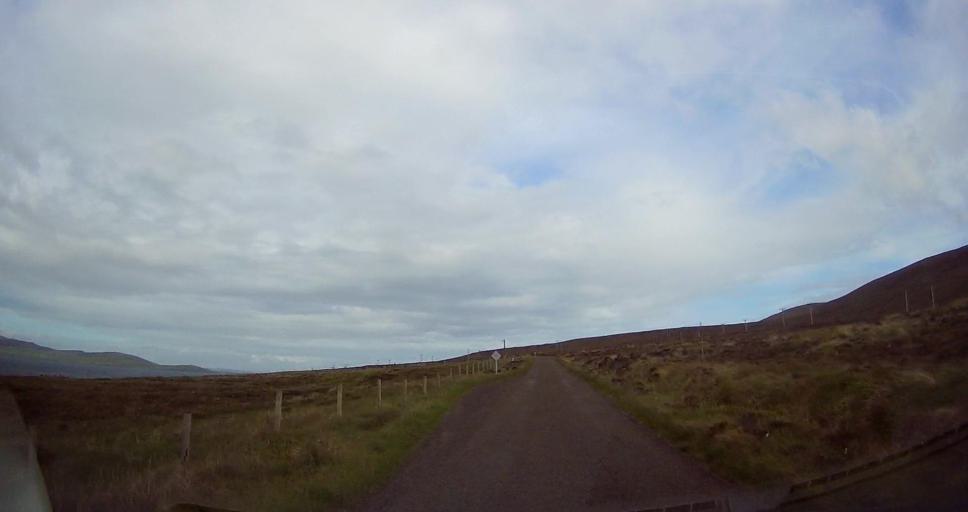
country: GB
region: Scotland
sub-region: Orkney Islands
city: Stromness
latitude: 58.9023
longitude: -3.2957
